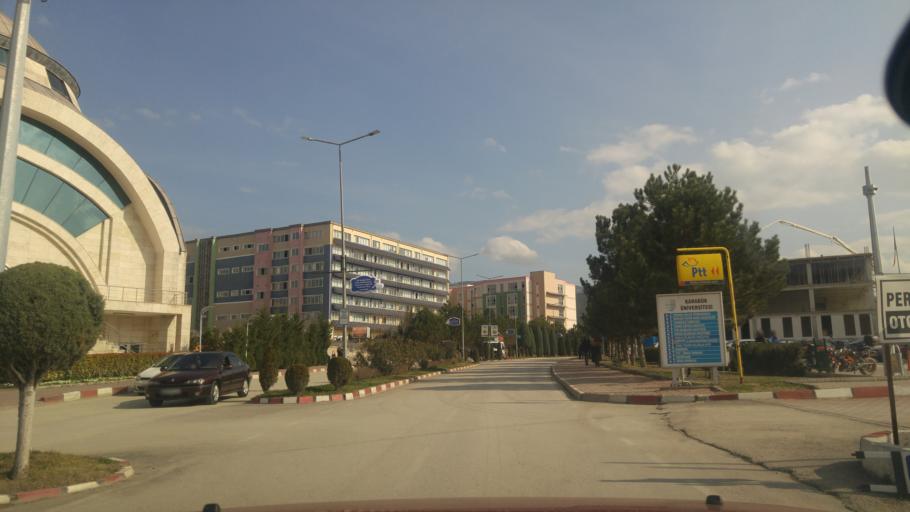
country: TR
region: Karabuk
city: Karabuk
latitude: 41.2118
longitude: 32.6541
